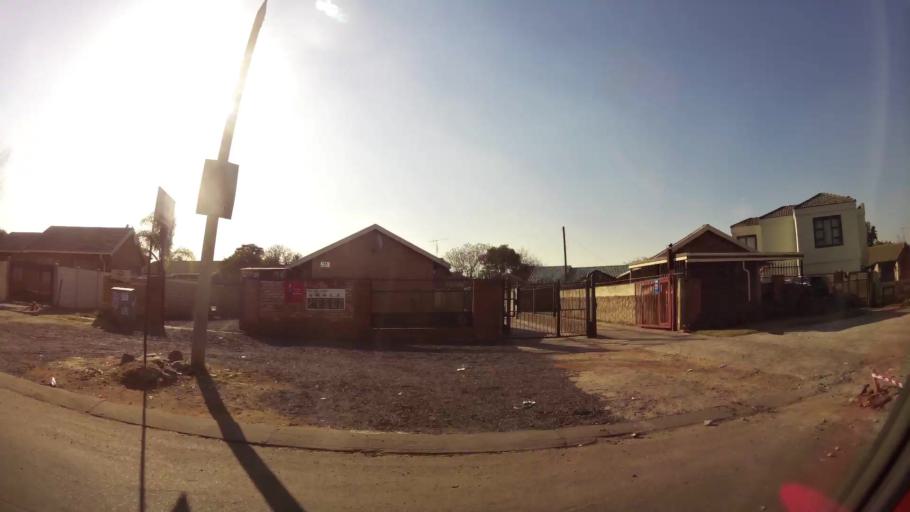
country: ZA
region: North-West
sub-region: Bojanala Platinum District Municipality
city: Rustenburg
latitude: -25.6573
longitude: 27.2265
